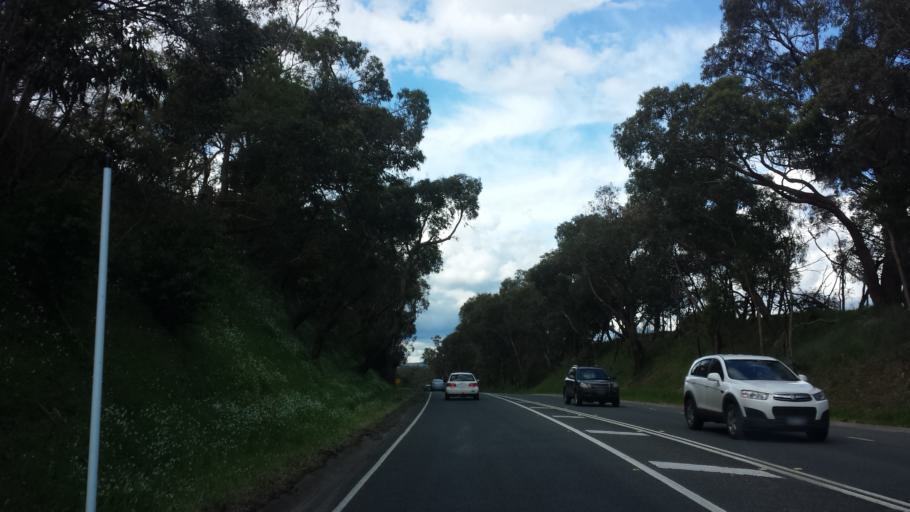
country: AU
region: Victoria
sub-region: Yarra Ranges
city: Belgrave South
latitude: -37.9611
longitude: 145.3617
